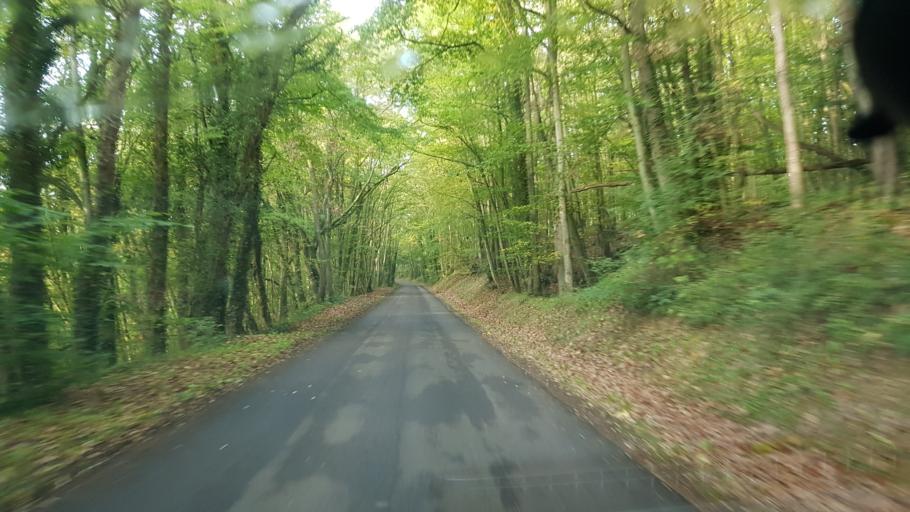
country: FR
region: Ile-de-France
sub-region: Departement de l'Essonne
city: Les Molieres
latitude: 48.6835
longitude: 2.0588
